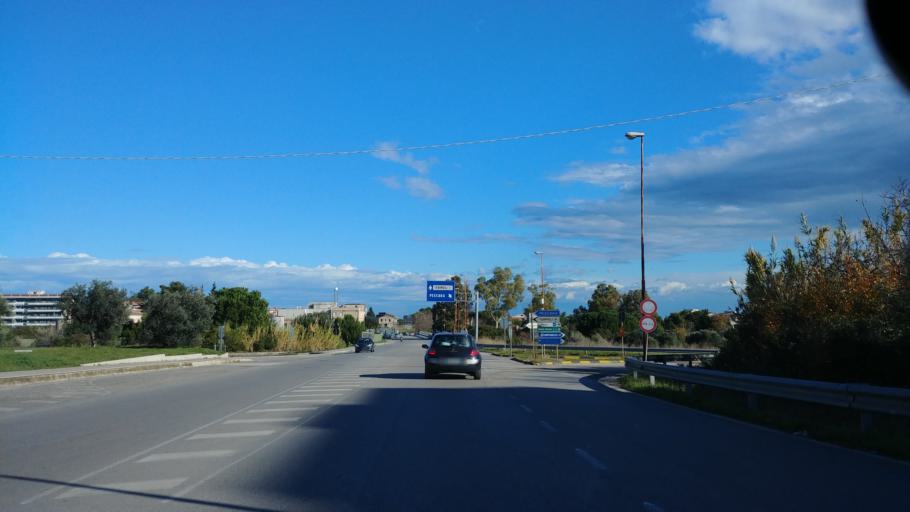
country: IT
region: Molise
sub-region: Provincia di Campobasso
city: Termoli
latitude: 41.9932
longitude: 14.9784
